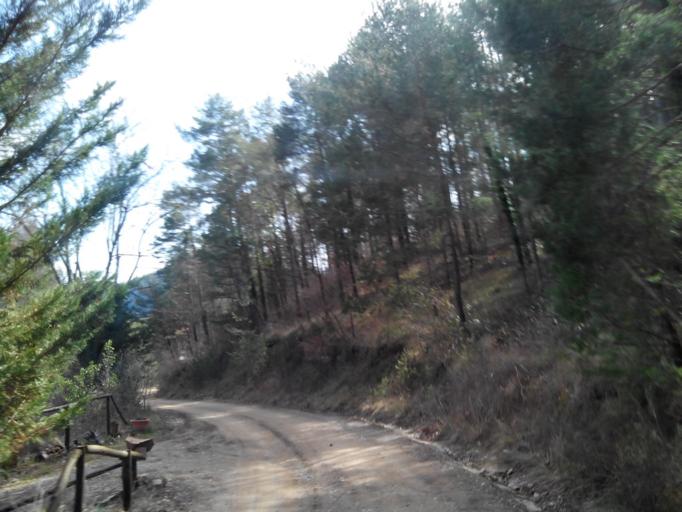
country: ES
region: Catalonia
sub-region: Provincia de Barcelona
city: Vilada
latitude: 42.1429
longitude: 1.9294
